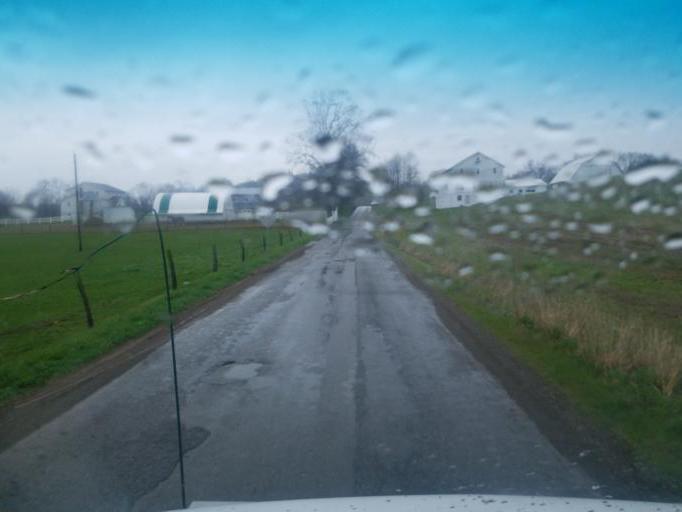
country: US
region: Ohio
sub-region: Holmes County
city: Millersburg
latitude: 40.6266
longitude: -81.8954
